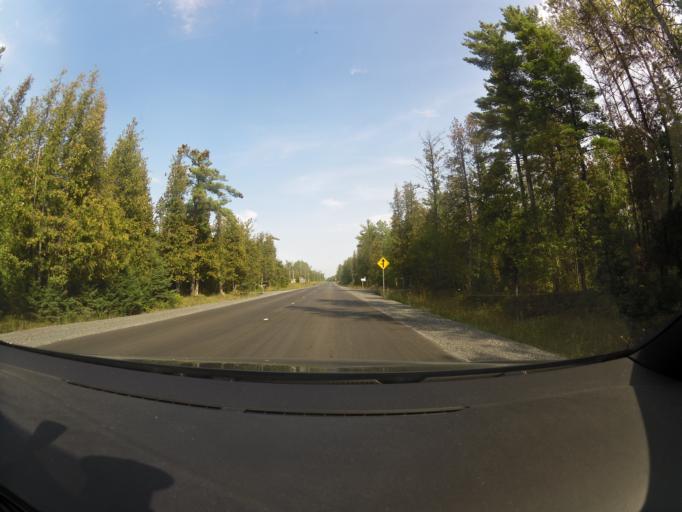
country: CA
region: Ontario
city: Carleton Place
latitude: 45.3355
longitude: -76.1570
